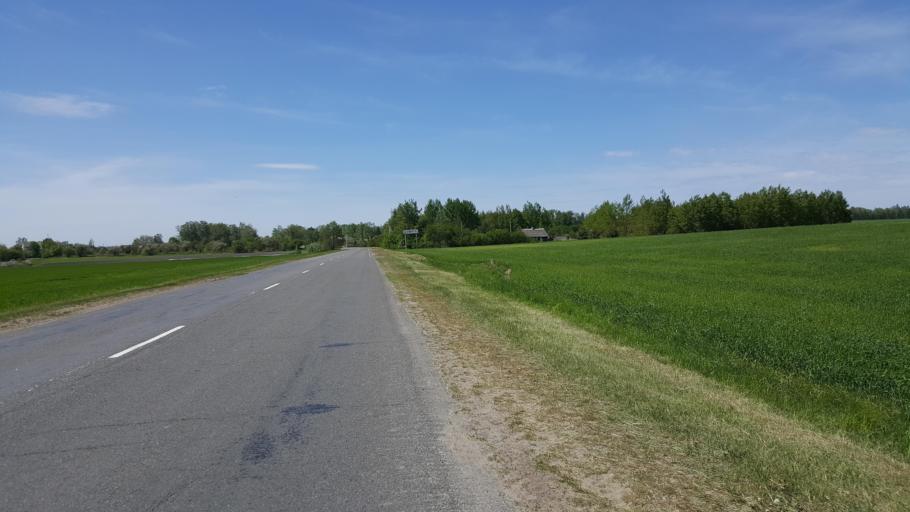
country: BY
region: Brest
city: Kobryn
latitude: 52.3507
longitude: 24.1937
